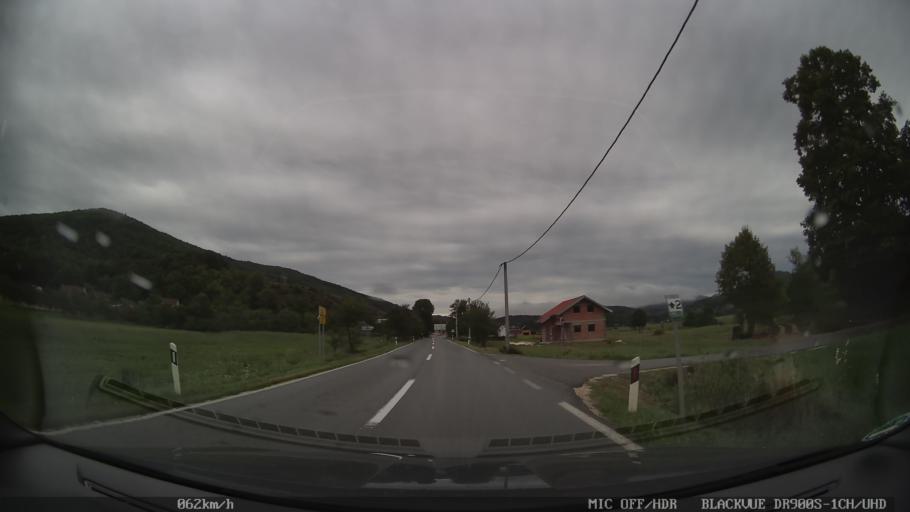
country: HR
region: Licko-Senjska
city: Otocac
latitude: 44.9057
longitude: 15.1720
